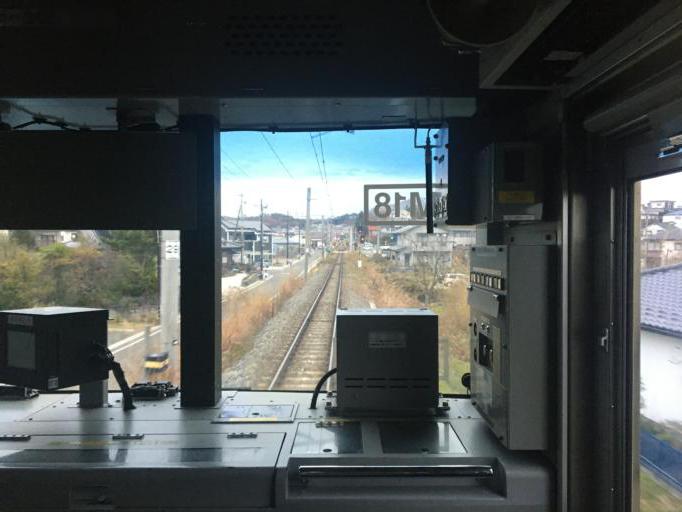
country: JP
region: Miyagi
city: Matsushima
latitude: 38.3806
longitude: 141.0716
